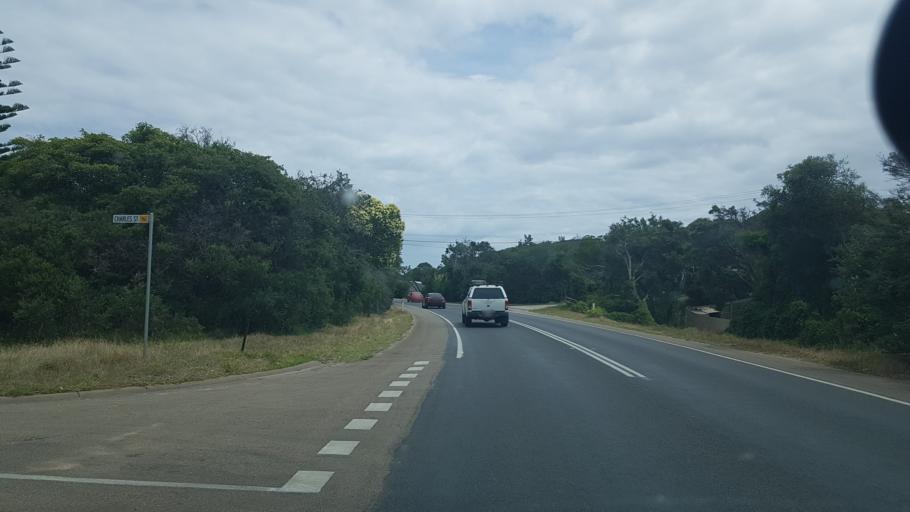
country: AU
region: Victoria
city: Rye
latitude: -38.3744
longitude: 144.8109
